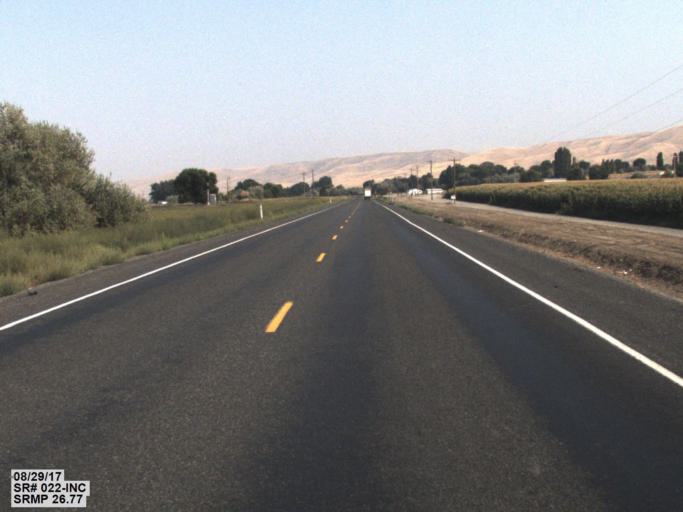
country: US
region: Washington
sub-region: Yakima County
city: Grandview
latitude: 46.1942
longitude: -119.9283
